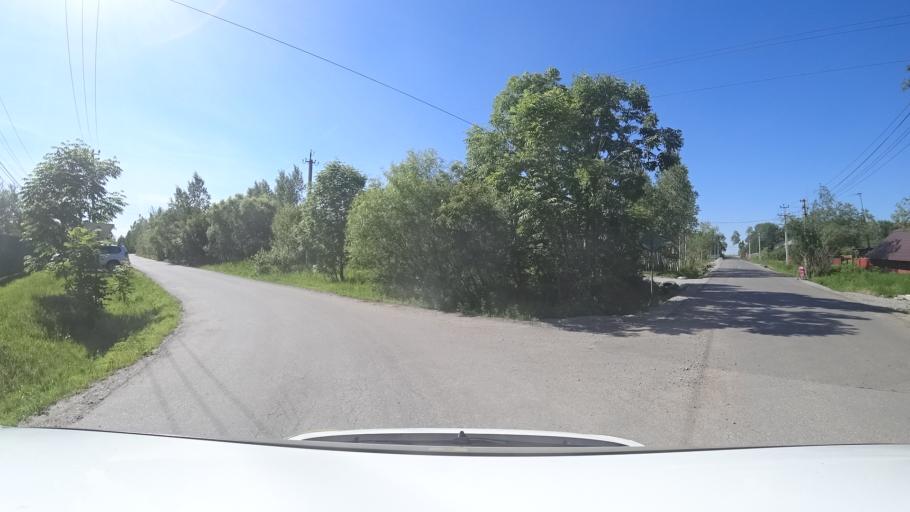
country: RU
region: Khabarovsk Krai
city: Topolevo
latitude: 48.5503
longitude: 135.1743
